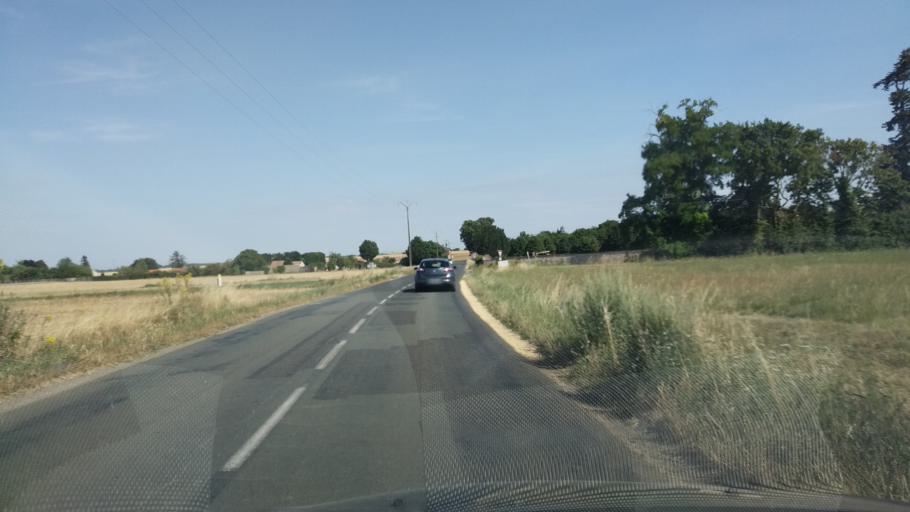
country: FR
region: Poitou-Charentes
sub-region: Departement de la Vienne
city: Vouille
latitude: 46.6813
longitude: 0.1746
